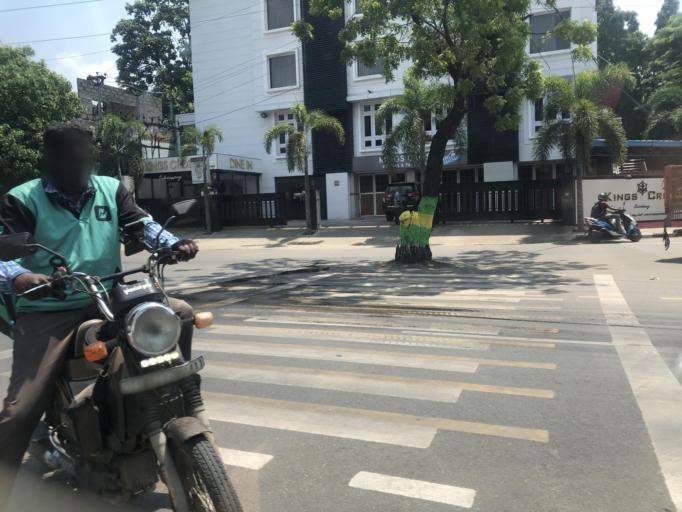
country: IN
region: Tamil Nadu
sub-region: Chennai
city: Gandhi Nagar
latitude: 12.9907
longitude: 80.2559
